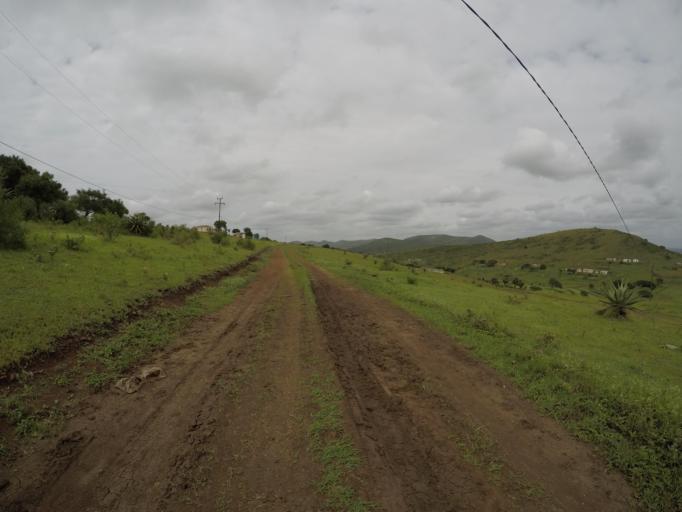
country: ZA
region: KwaZulu-Natal
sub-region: uThungulu District Municipality
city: Empangeni
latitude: -28.6165
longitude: 31.8954
